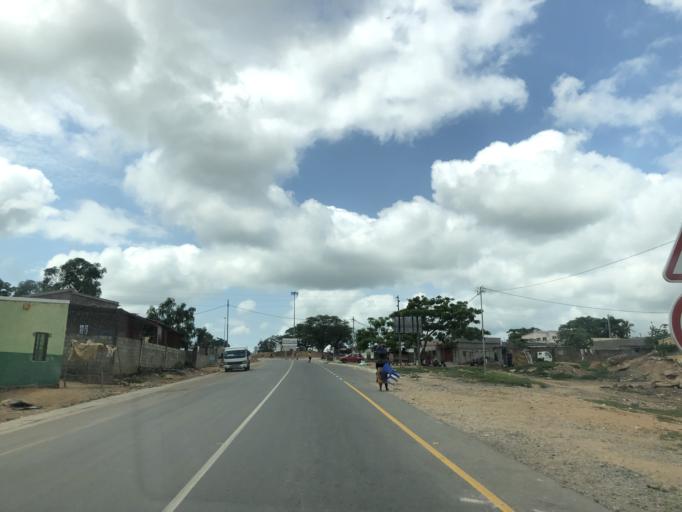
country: AO
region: Cuanza Norte
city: N'dalatando
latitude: -9.6807
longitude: 14.4733
